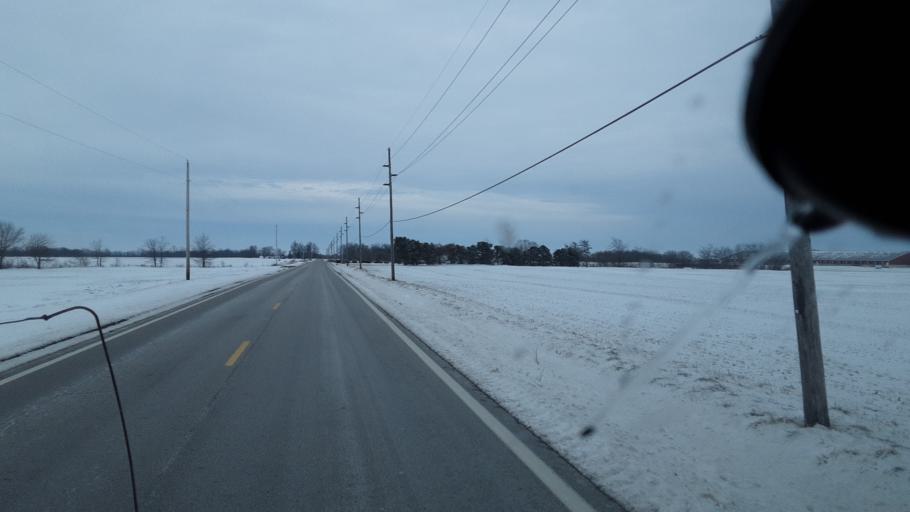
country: US
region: Ohio
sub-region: Madison County
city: Mount Sterling
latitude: 39.6848
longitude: -83.2063
